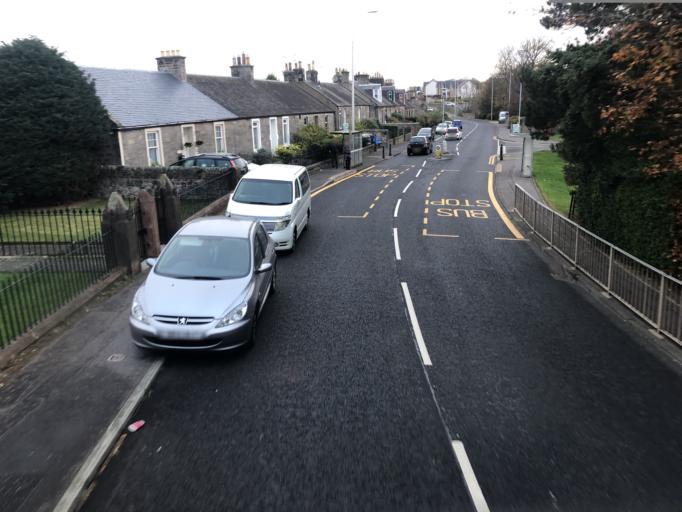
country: GB
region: Scotland
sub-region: Midlothian
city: Loanhead
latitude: 55.8833
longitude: -3.1568
